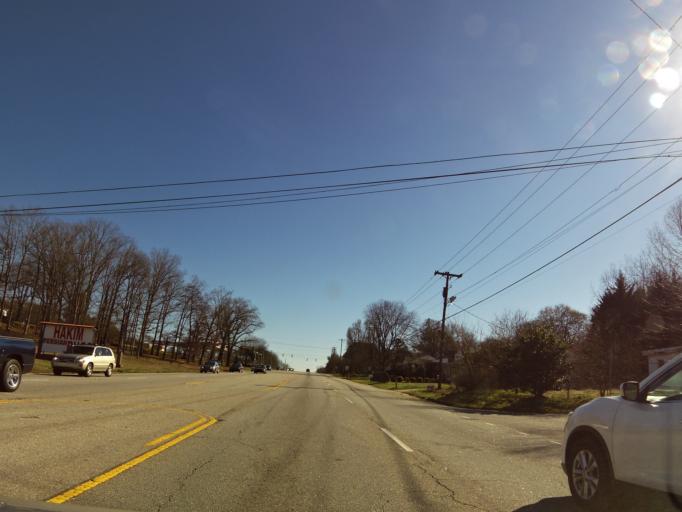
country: US
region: South Carolina
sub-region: Greenville County
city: Sans Souci
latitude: 34.8998
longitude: -82.4148
